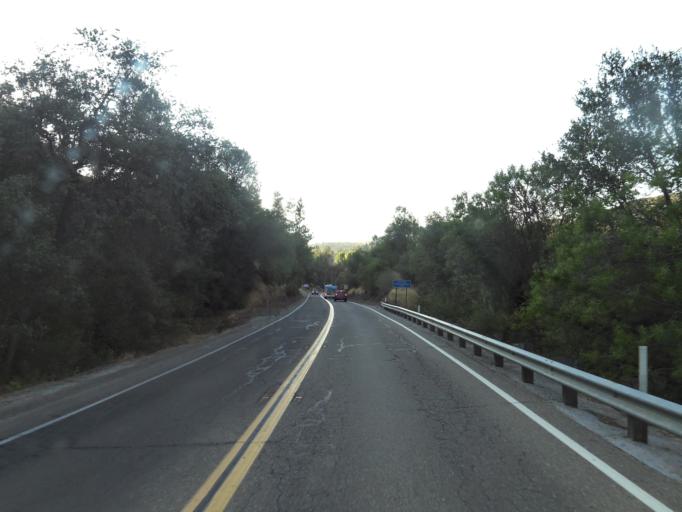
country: US
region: California
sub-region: Mariposa County
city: Mariposa
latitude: 37.4794
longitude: -119.9615
